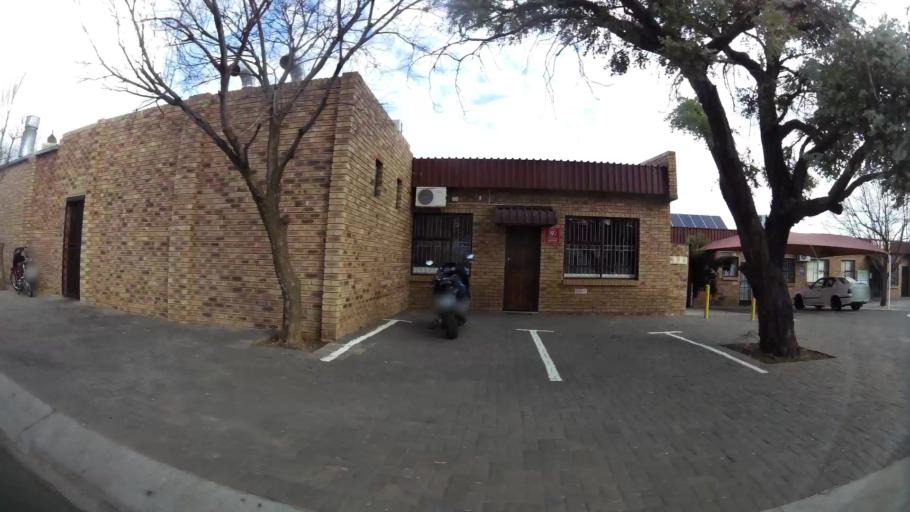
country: ZA
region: Orange Free State
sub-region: Mangaung Metropolitan Municipality
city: Bloemfontein
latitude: -29.0754
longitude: 26.1973
